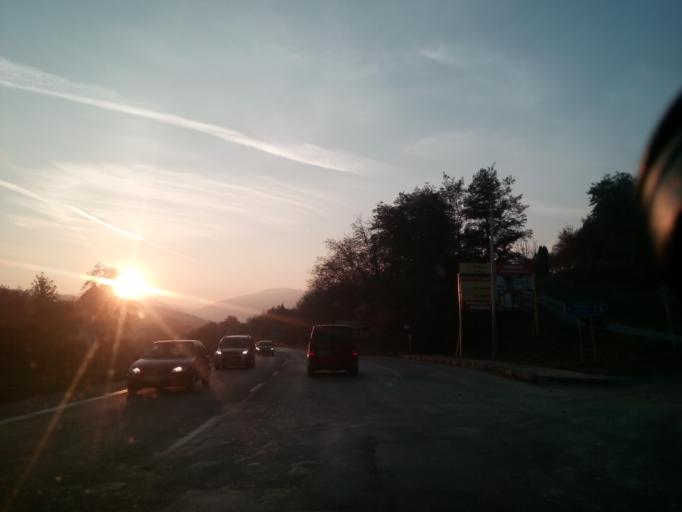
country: SK
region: Presovsky
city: Sabinov
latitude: 49.0223
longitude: 20.9939
